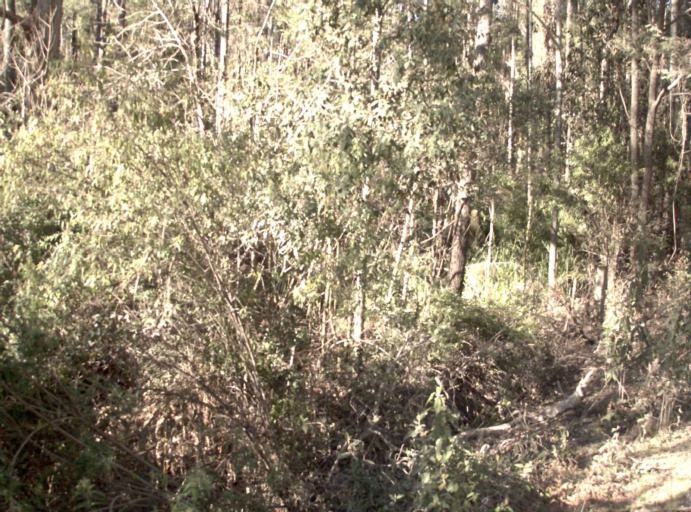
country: AU
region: Tasmania
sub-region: Launceston
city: Mayfield
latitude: -41.1932
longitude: 147.1603
